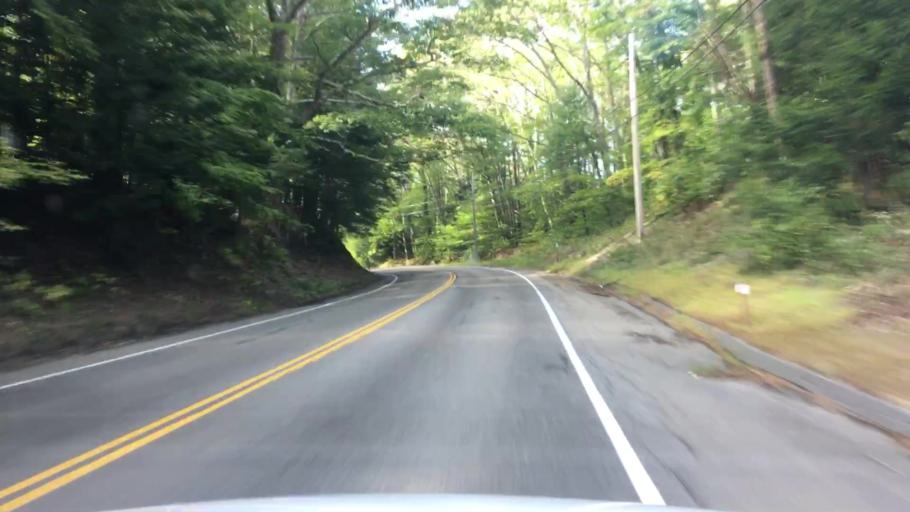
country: US
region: Maine
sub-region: Sagadahoc County
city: Topsham
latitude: 43.9333
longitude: -70.0106
